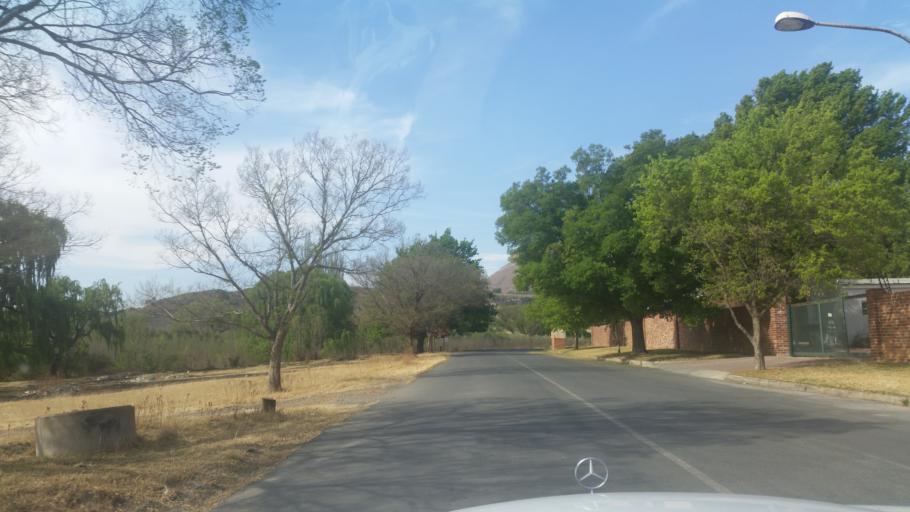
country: ZA
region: Orange Free State
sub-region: Thabo Mofutsanyana District Municipality
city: Harrismith
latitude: -28.2629
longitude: 29.1190
